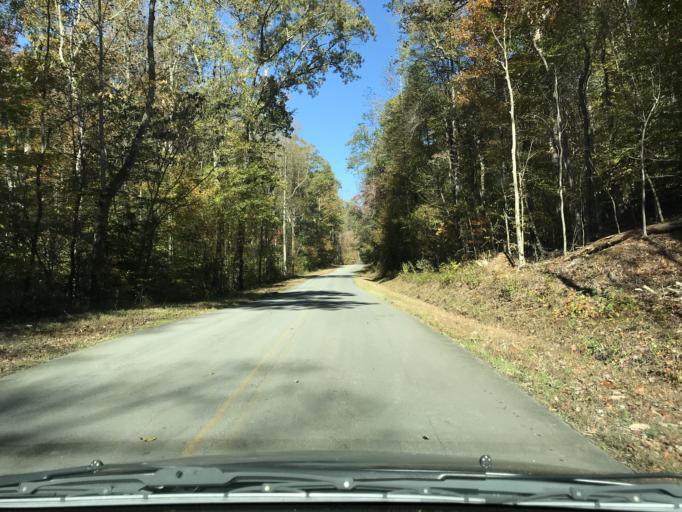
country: US
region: Georgia
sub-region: Dade County
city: Trenton
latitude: 34.9061
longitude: -85.4652
